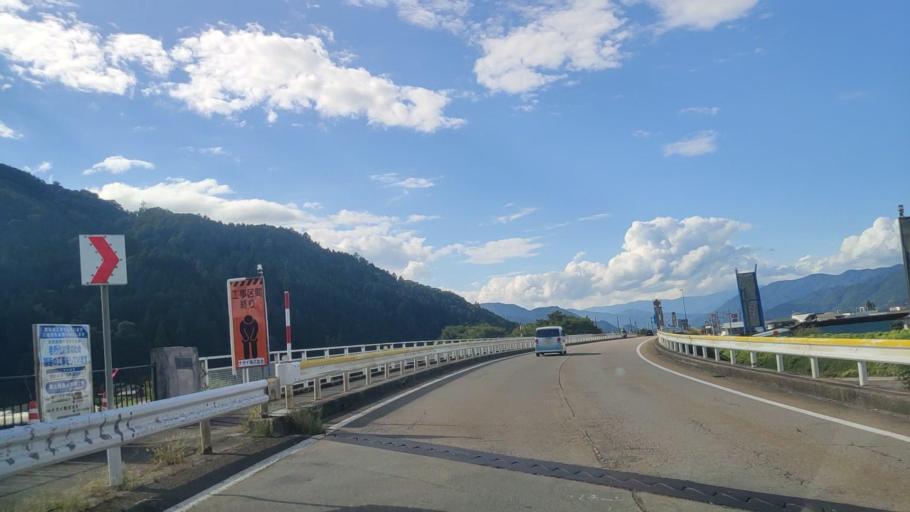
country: JP
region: Gifu
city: Takayama
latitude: 36.2091
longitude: 137.2117
